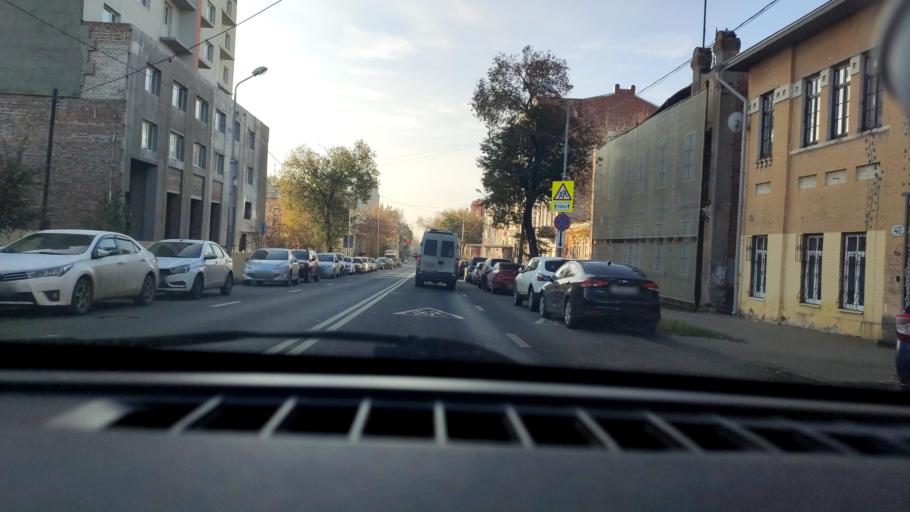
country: RU
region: Samara
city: Rozhdestveno
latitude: 53.1824
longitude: 50.0856
